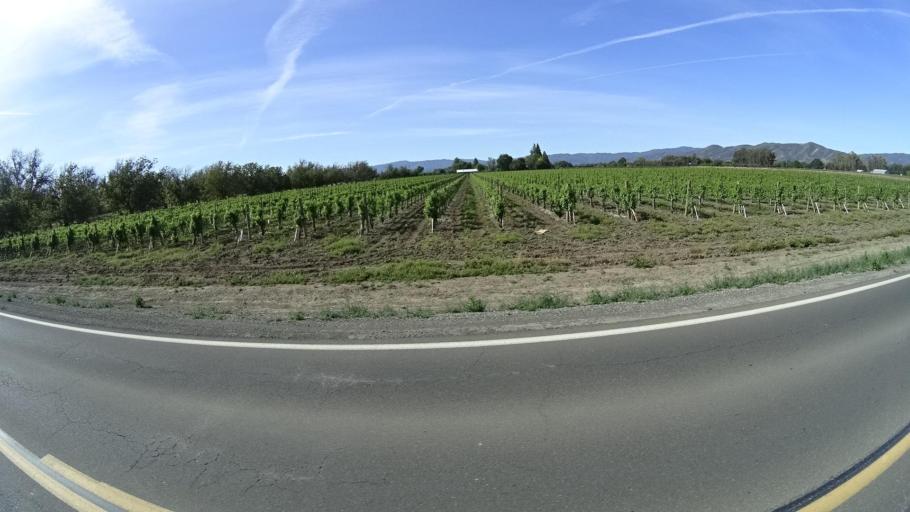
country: US
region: California
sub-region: Lake County
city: Lakeport
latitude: 39.0149
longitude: -122.8840
